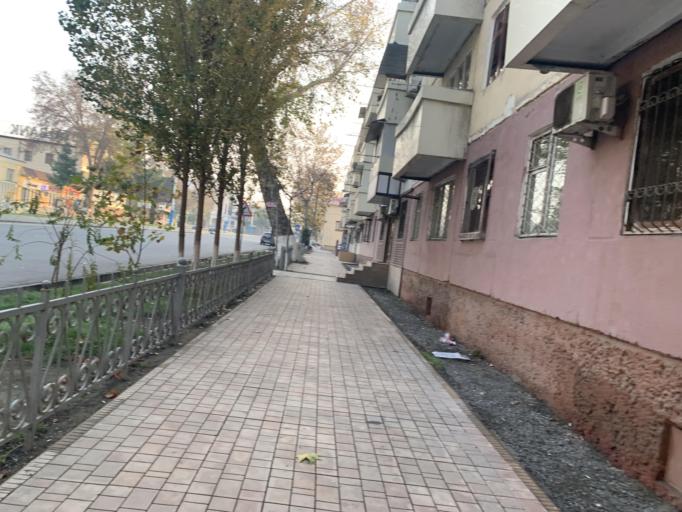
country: UZ
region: Fergana
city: Qo`qon
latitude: 40.5282
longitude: 70.9391
